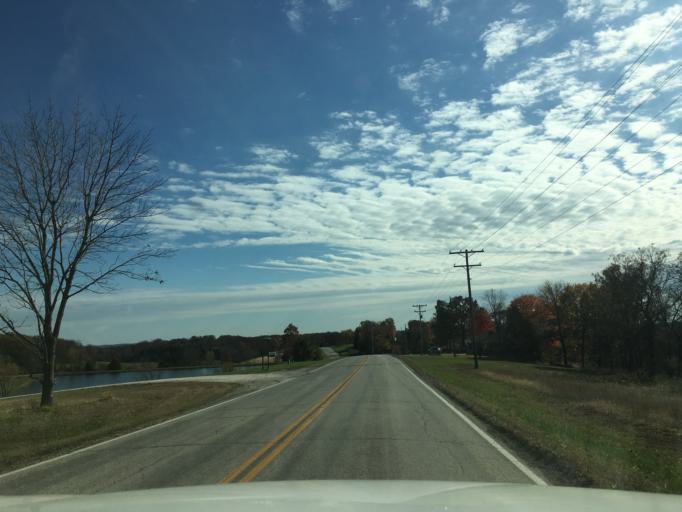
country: US
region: Missouri
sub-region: Osage County
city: Linn
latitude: 38.4441
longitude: -91.8377
